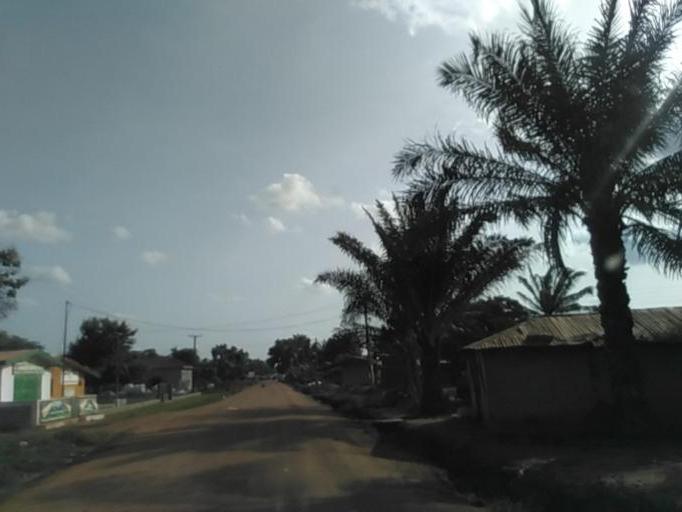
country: GH
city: Akropong
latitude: 6.0931
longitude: 0.1984
